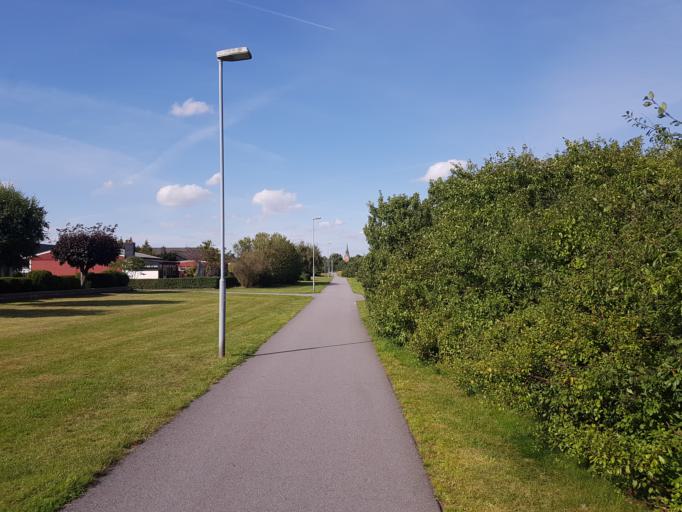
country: SE
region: Skane
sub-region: Sjobo Kommun
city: Sjoebo
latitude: 55.6385
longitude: 13.6996
